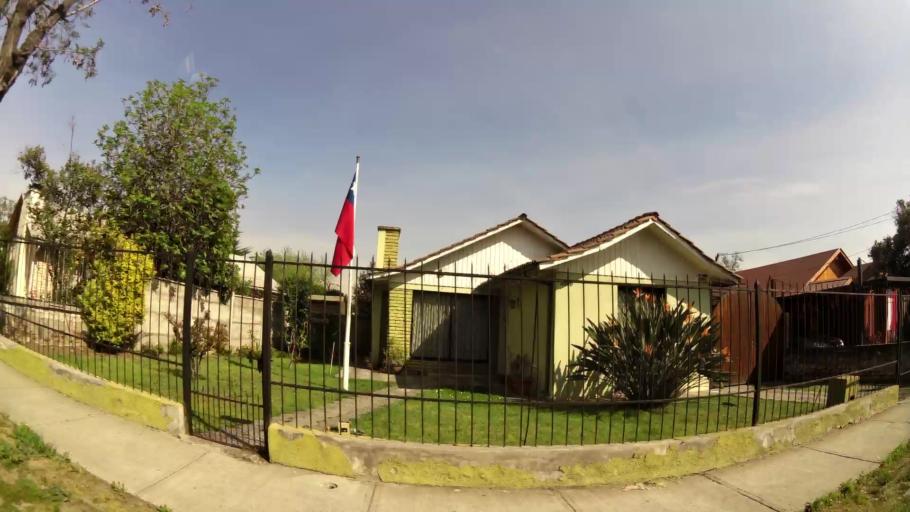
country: CL
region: Santiago Metropolitan
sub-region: Provincia de Santiago
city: Villa Presidente Frei, Nunoa, Santiago, Chile
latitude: -33.4917
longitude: -70.5921
